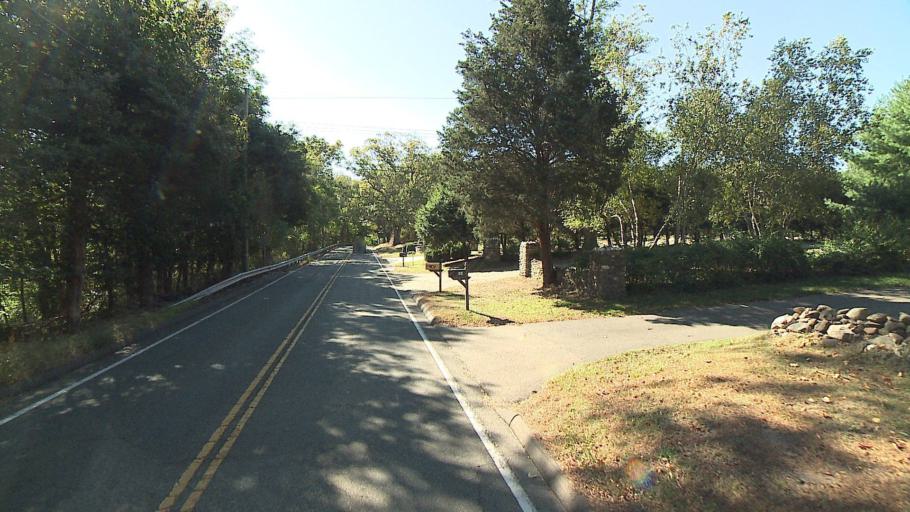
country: US
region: Connecticut
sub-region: New Haven County
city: Orange
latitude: 41.3055
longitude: -73.0190
